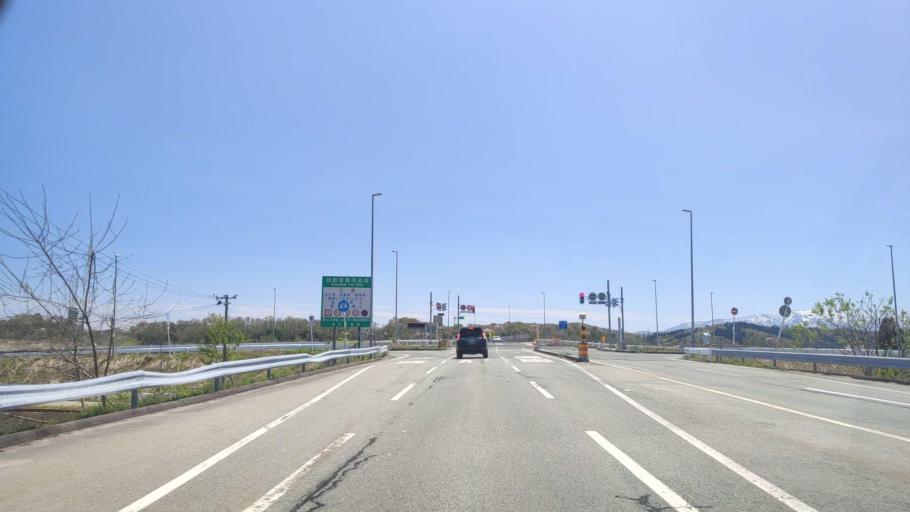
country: JP
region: Yamagata
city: Shinjo
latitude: 38.7424
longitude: 140.2949
